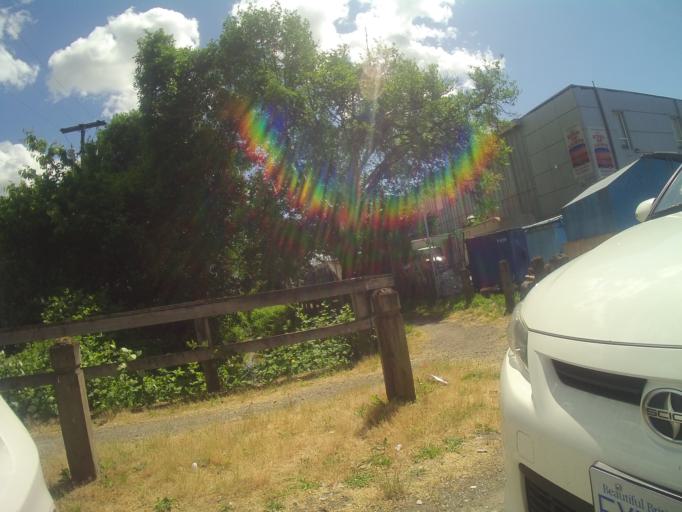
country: CA
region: British Columbia
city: Richmond
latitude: 49.1911
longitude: -123.0848
